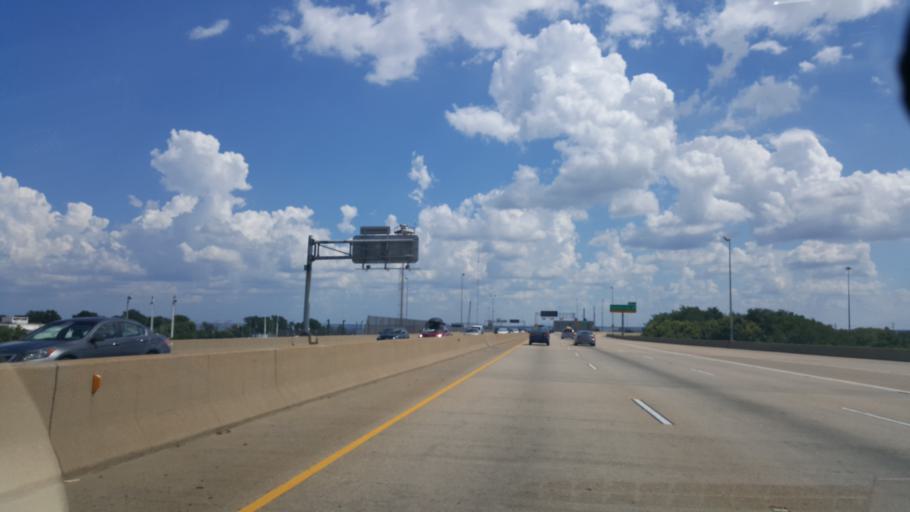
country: US
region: Virginia
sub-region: City of Newport News
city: Newport News
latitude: 36.9710
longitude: -76.4179
